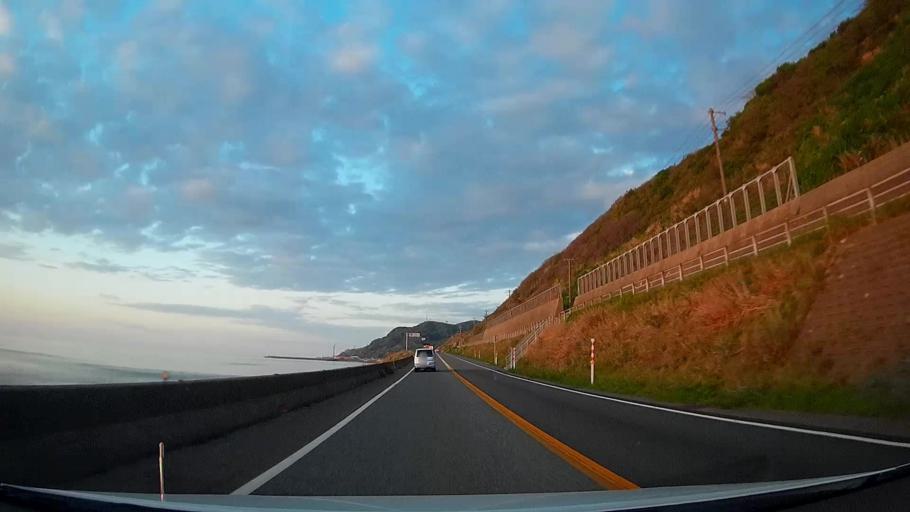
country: JP
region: Niigata
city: Joetsu
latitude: 37.1491
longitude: 138.0693
